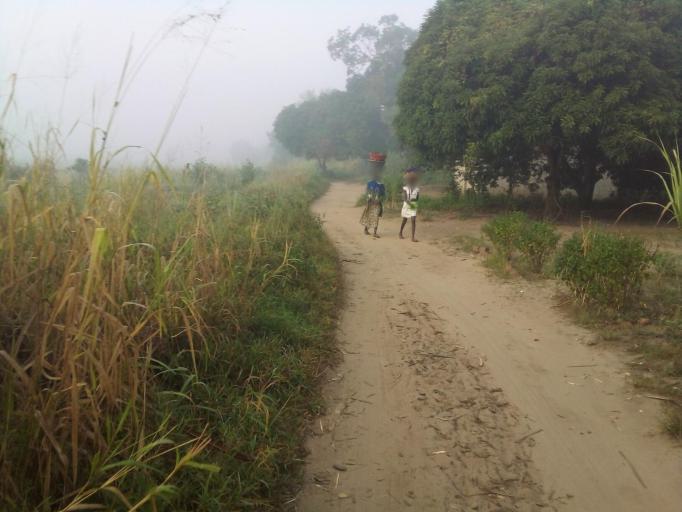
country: MZ
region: Zambezia
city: Quelimane
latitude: -17.5899
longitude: 36.6869
